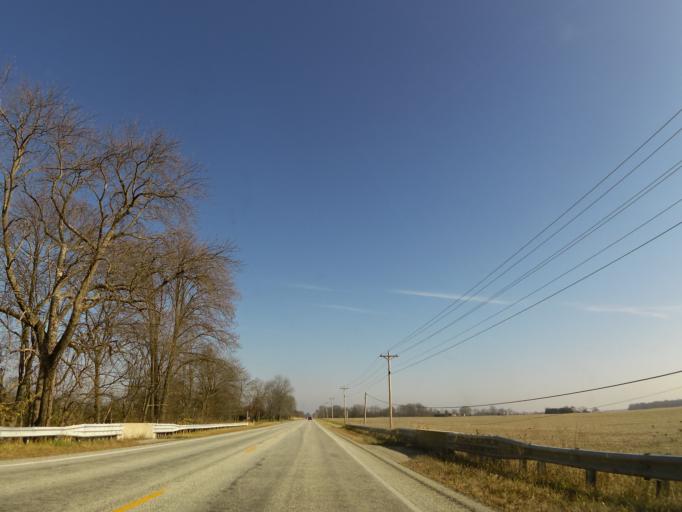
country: US
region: Indiana
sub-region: Shelby County
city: Shelbyville
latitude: 39.5365
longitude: -85.7122
